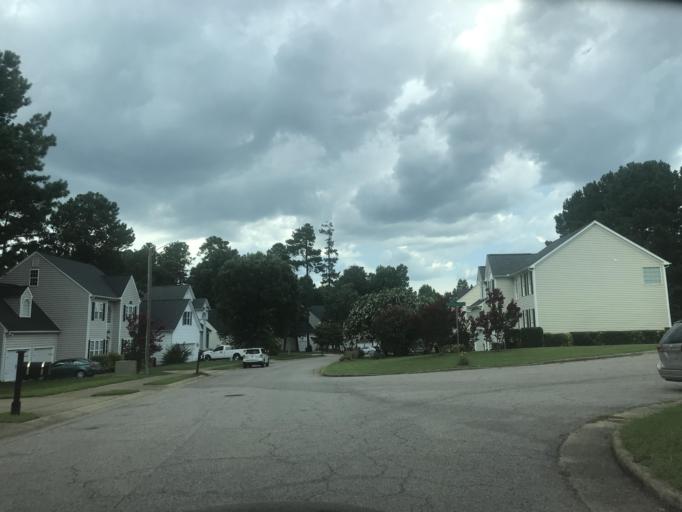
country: US
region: North Carolina
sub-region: Wake County
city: Knightdale
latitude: 35.8362
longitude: -78.5584
